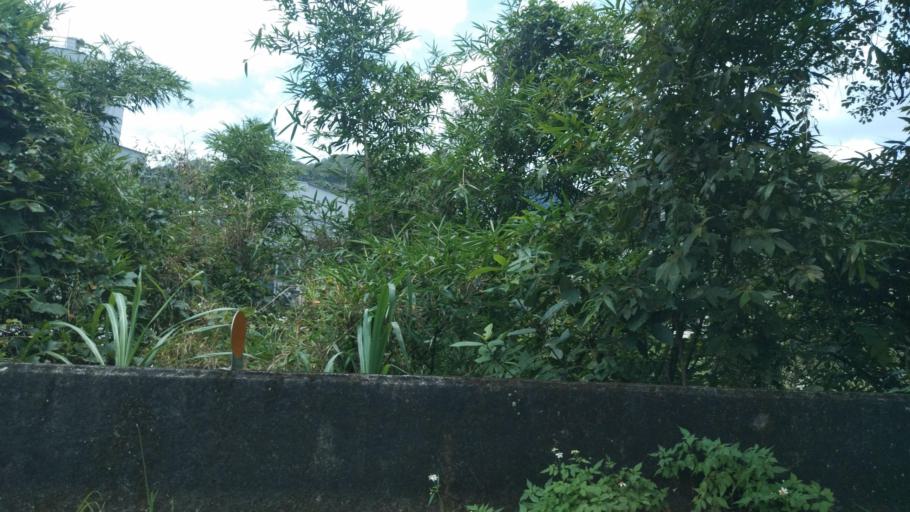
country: TW
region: Taipei
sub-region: Taipei
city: Banqiao
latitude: 24.9340
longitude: 121.4582
